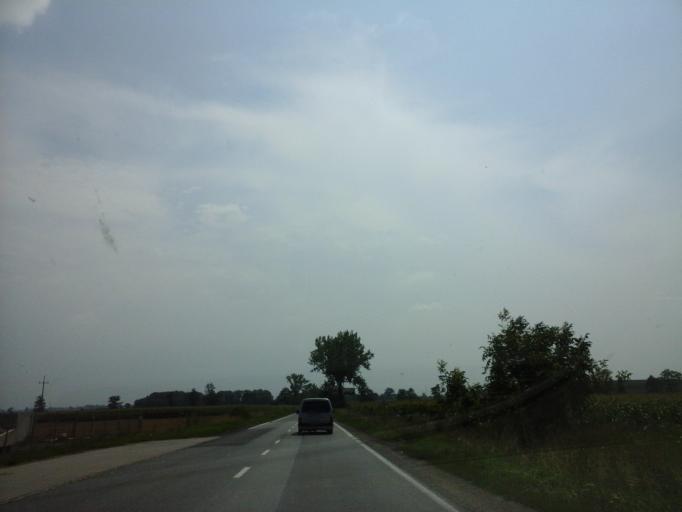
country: PL
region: Lower Silesian Voivodeship
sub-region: Powiat wroclawski
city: Zorawina
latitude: 50.9780
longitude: 17.0706
